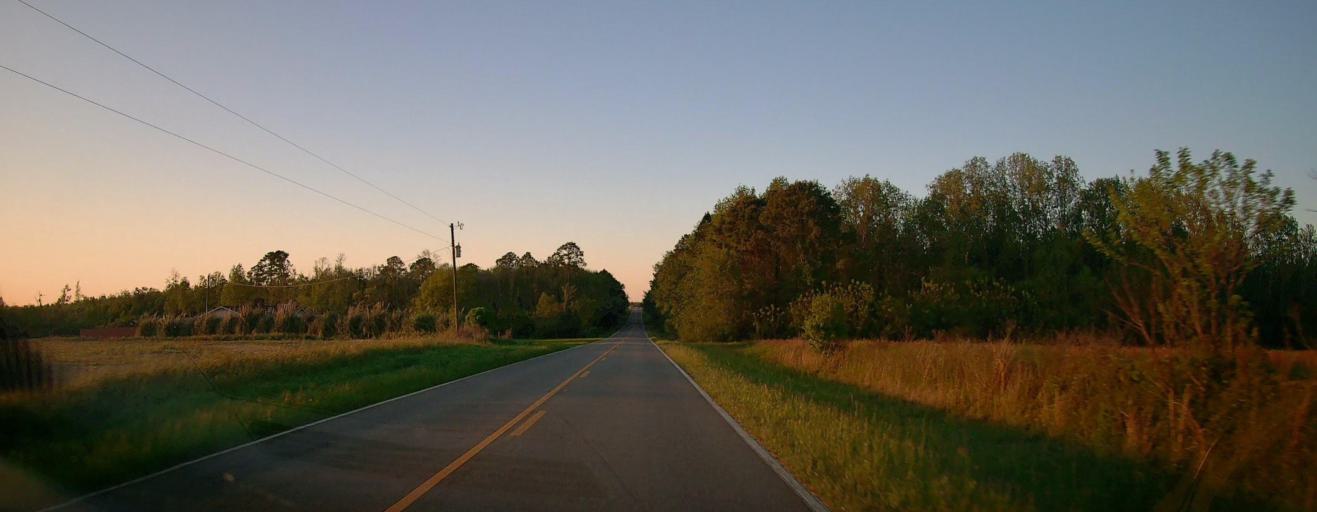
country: US
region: Georgia
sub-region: Ben Hill County
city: Fitzgerald
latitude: 31.7341
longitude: -83.3097
